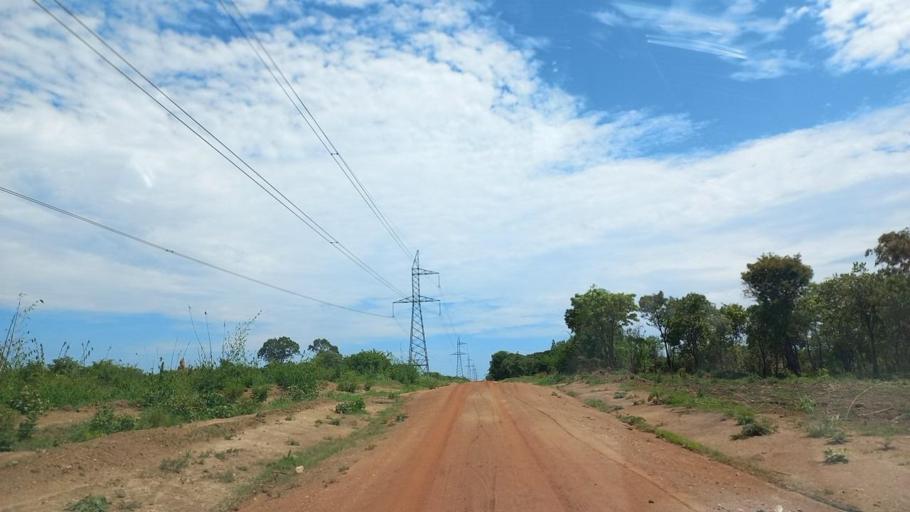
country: ZM
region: Copperbelt
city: Kitwe
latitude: -12.8262
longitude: 28.3489
